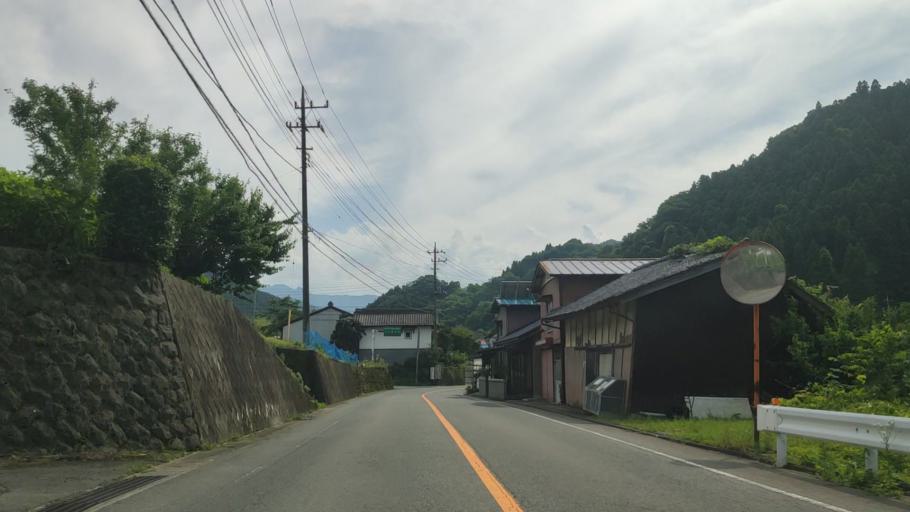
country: JP
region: Gunma
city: Tomioka
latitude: 36.1847
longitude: 138.7472
